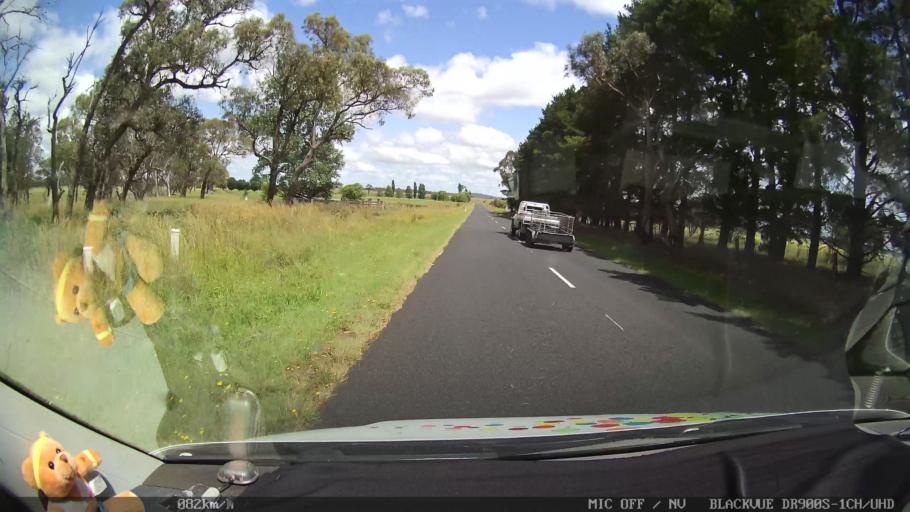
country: AU
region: New South Wales
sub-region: Glen Innes Severn
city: Glen Innes
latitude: -29.6859
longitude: 151.7024
